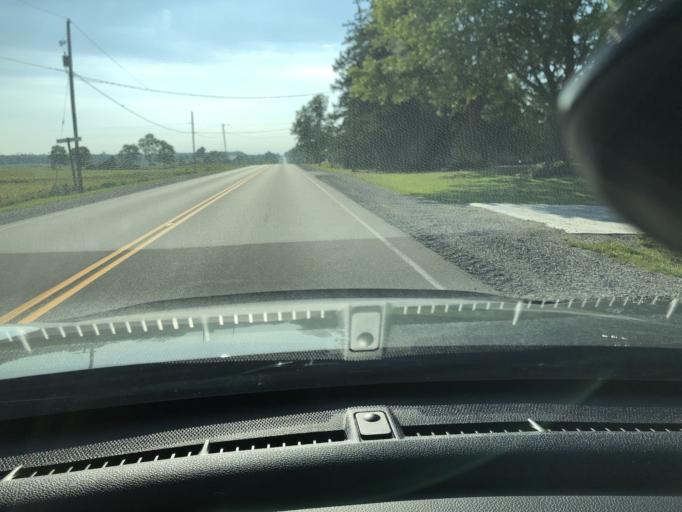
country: CA
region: Ontario
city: Stratford
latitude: 43.4243
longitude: -80.7864
